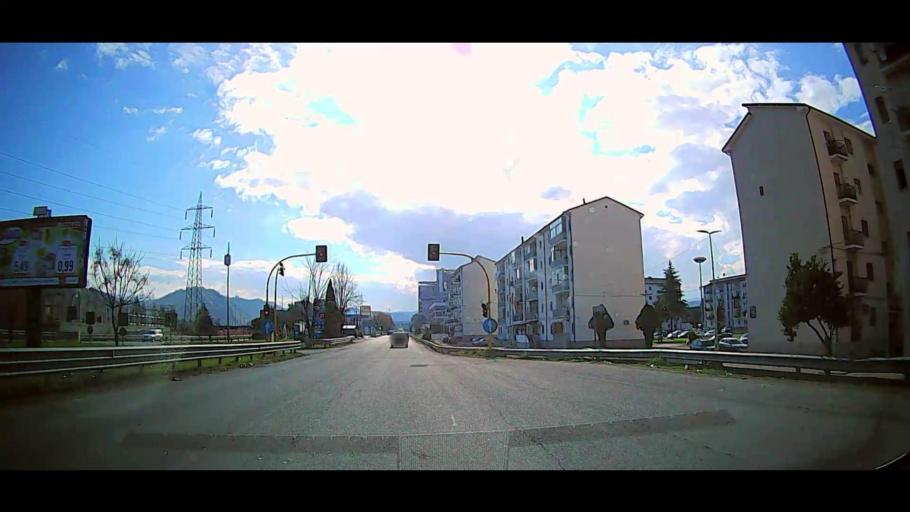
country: IT
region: Calabria
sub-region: Provincia di Cosenza
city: Cosenza
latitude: 39.3255
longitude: 16.2553
